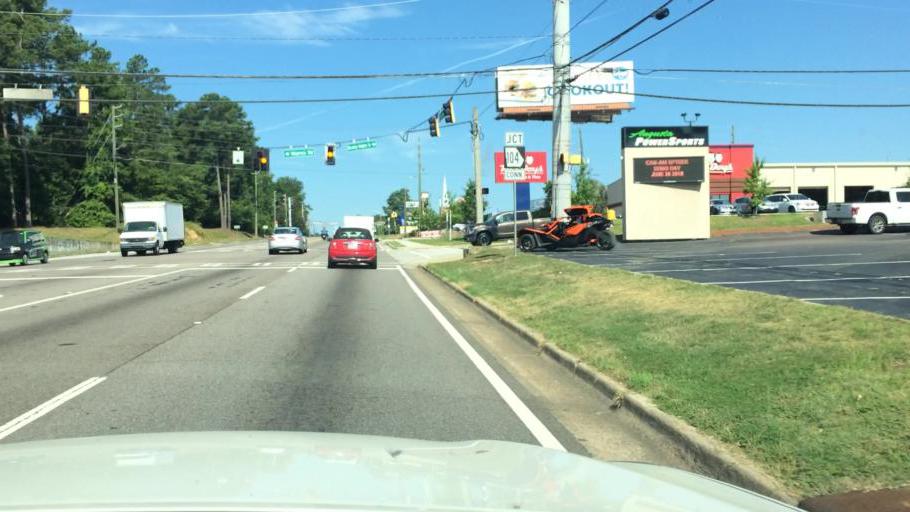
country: US
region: Georgia
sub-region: Columbia County
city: Martinez
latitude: 33.5140
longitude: -82.0558
